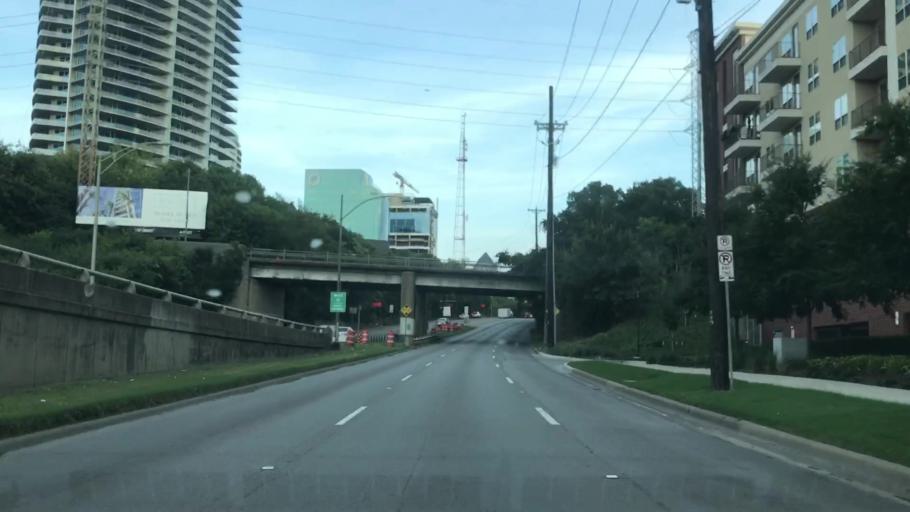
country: US
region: Texas
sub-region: Dallas County
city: Dallas
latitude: 32.7978
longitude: -96.8139
